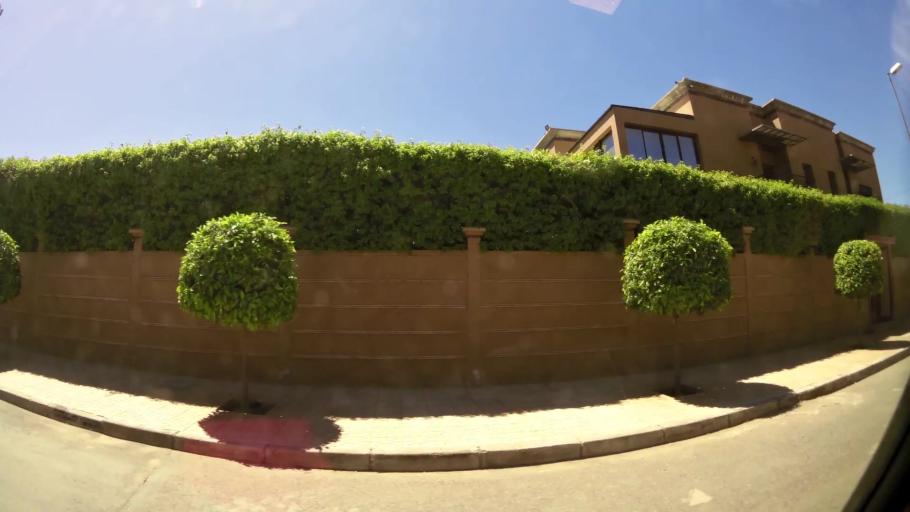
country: MA
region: Marrakech-Tensift-Al Haouz
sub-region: Marrakech
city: Marrakesh
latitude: 31.6543
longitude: -7.9857
